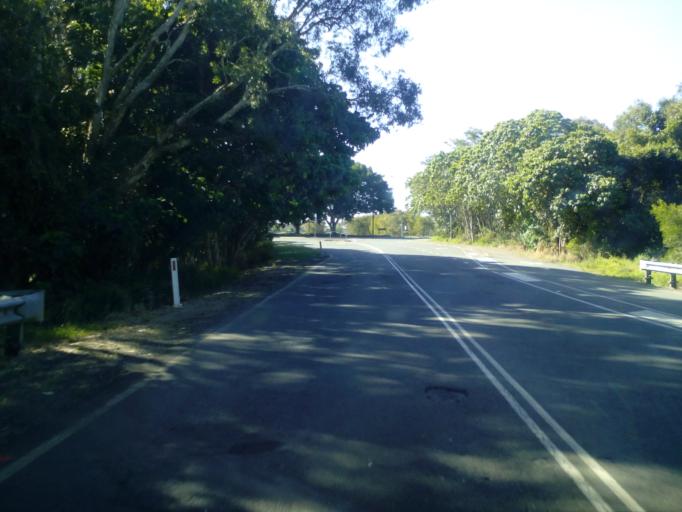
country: AU
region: New South Wales
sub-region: Tweed
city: Kingscliff
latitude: -28.2594
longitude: 153.5704
